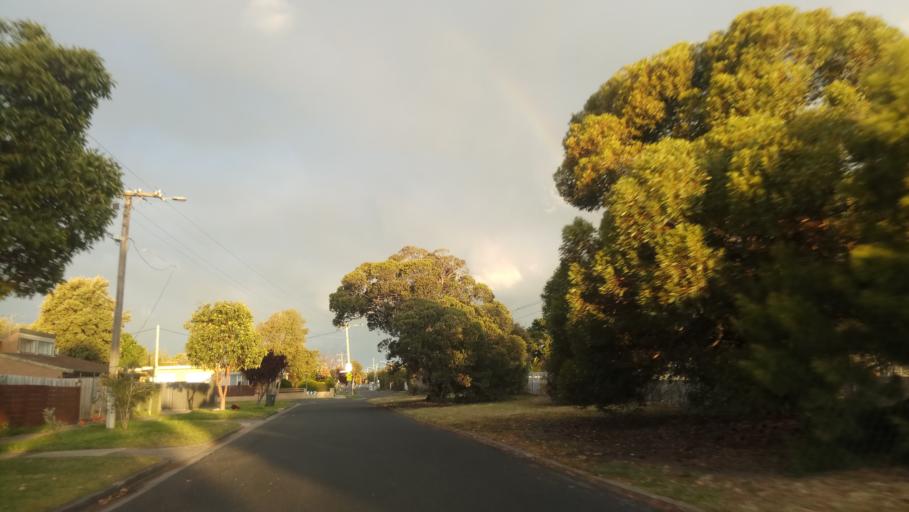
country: AU
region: Victoria
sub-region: Hobsons Bay
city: Altona
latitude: -37.8661
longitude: 144.8214
